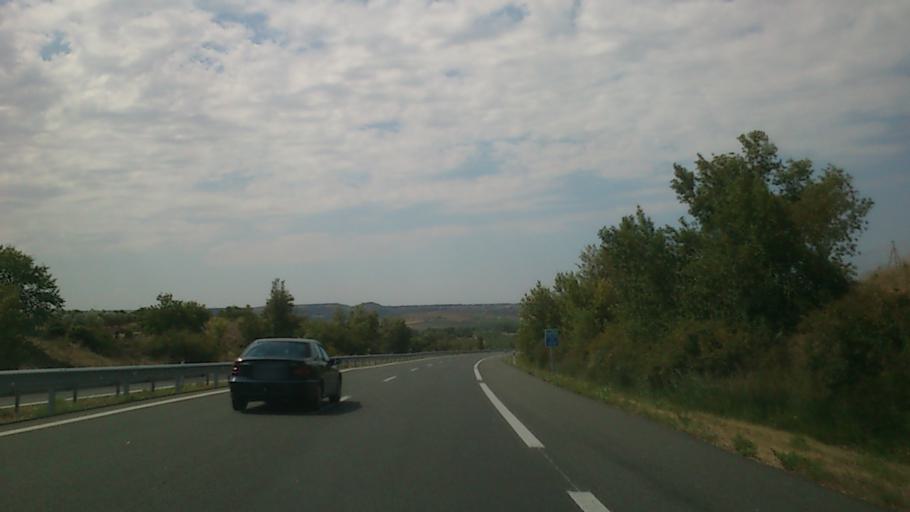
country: ES
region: La Rioja
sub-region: Provincia de La Rioja
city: Torremontalbo
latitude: 42.4788
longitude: -2.6775
